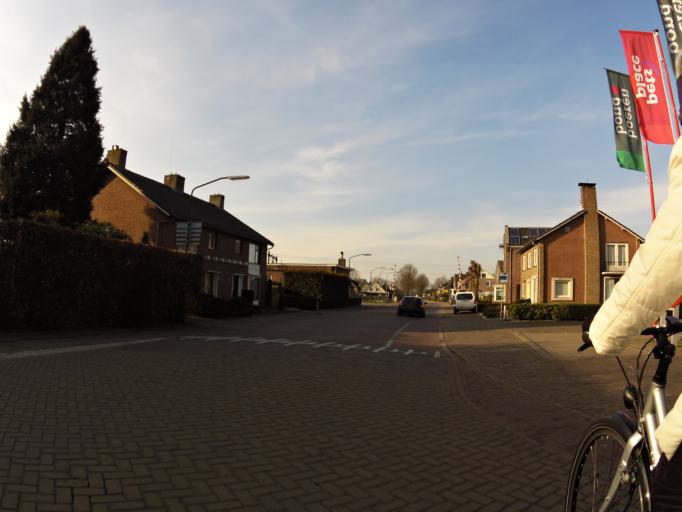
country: NL
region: North Brabant
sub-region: Gemeente Haaren
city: Haaren
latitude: 51.6359
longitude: 5.2329
